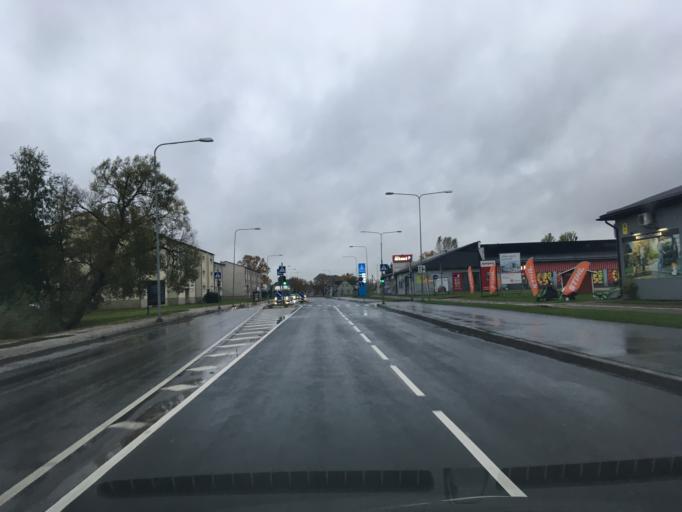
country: EE
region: Paernumaa
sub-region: Paernu linn
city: Parnu
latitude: 58.4049
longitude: 24.4930
